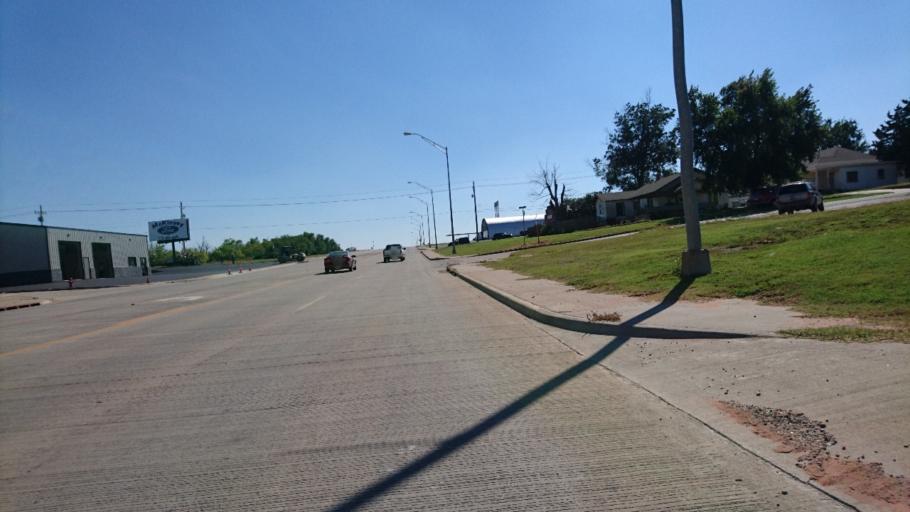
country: US
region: Oklahoma
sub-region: Custer County
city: Clinton
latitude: 35.5097
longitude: -98.9649
